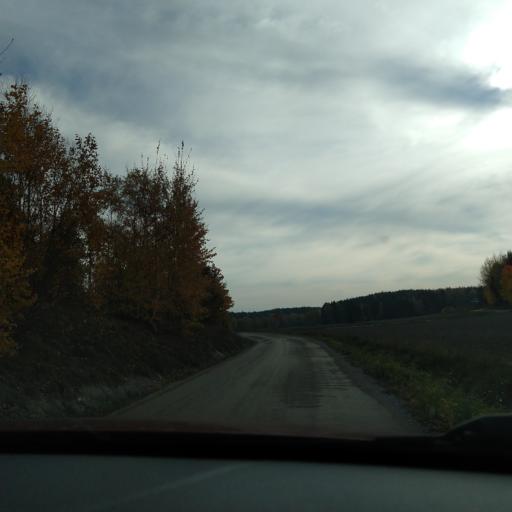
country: SE
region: Stockholm
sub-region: Vallentuna Kommun
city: Vallentuna
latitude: 59.5402
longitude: 18.0189
